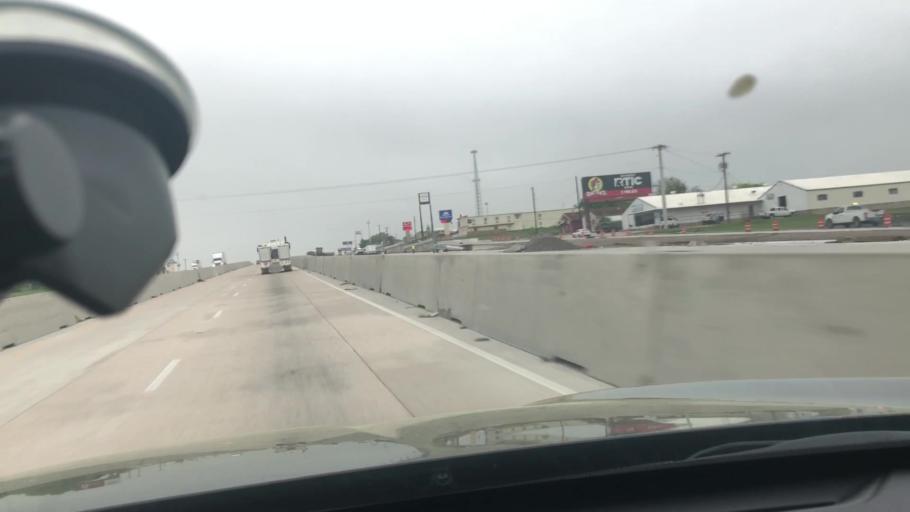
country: US
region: Texas
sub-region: Bell County
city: Temple
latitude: 31.1081
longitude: -97.3576
